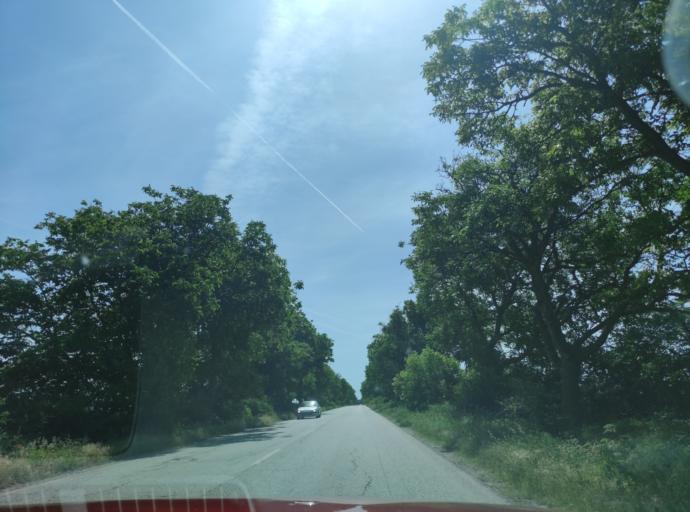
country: BG
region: Pleven
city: Iskur
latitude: 43.4443
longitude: 24.3345
